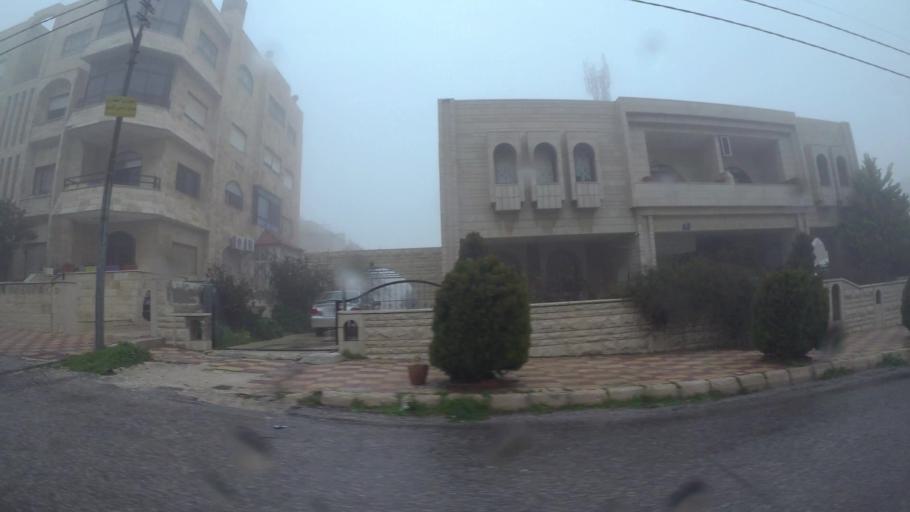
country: JO
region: Amman
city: Al Jubayhah
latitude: 32.0063
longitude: 35.8884
